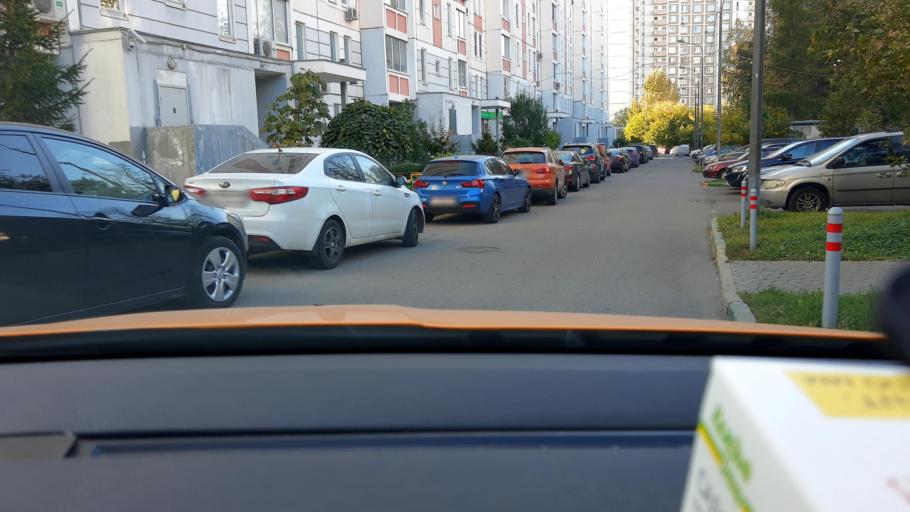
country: RU
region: Moskovskaya
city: Marfino
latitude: 55.7135
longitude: 37.3980
